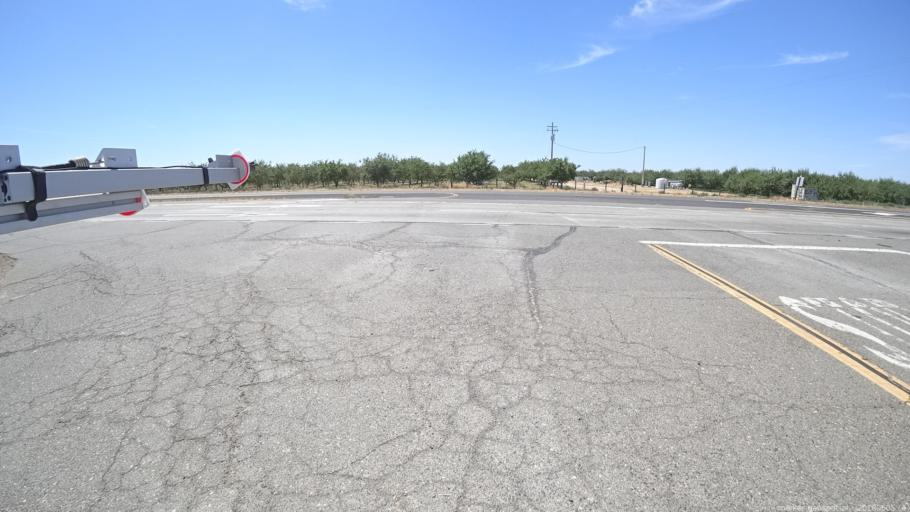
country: US
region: California
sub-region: Merced County
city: Dos Palos
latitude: 37.0837
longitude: -120.4553
